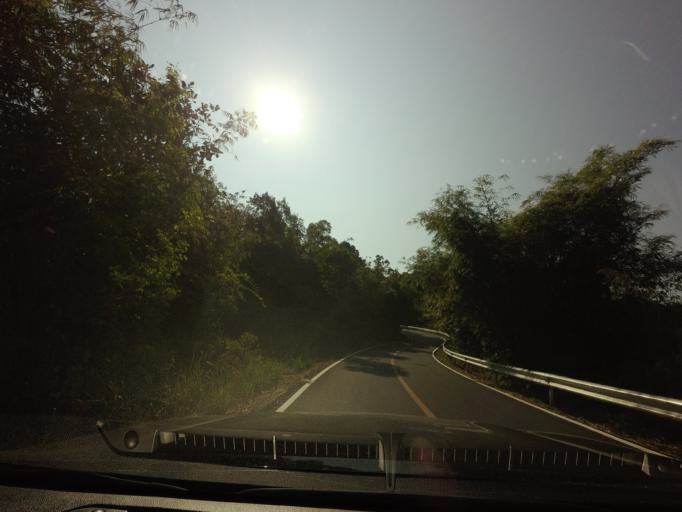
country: TH
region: Kanchanaburi
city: Thong Pha Phum
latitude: 14.6870
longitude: 98.4150
